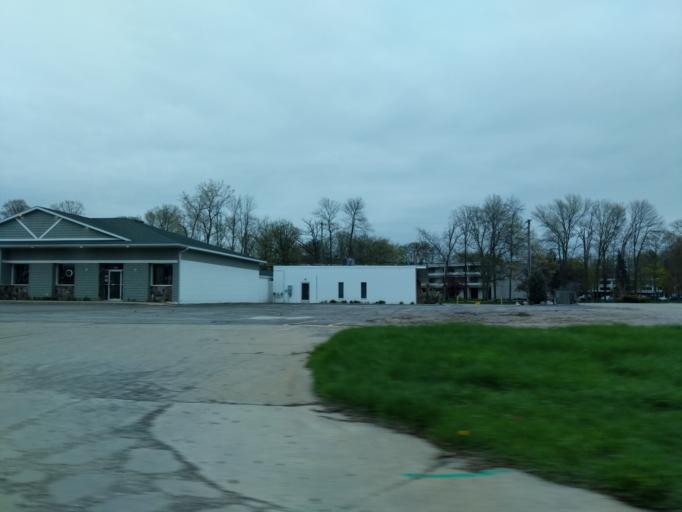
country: US
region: Michigan
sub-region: Midland County
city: Midland
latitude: 43.6214
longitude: -84.2216
